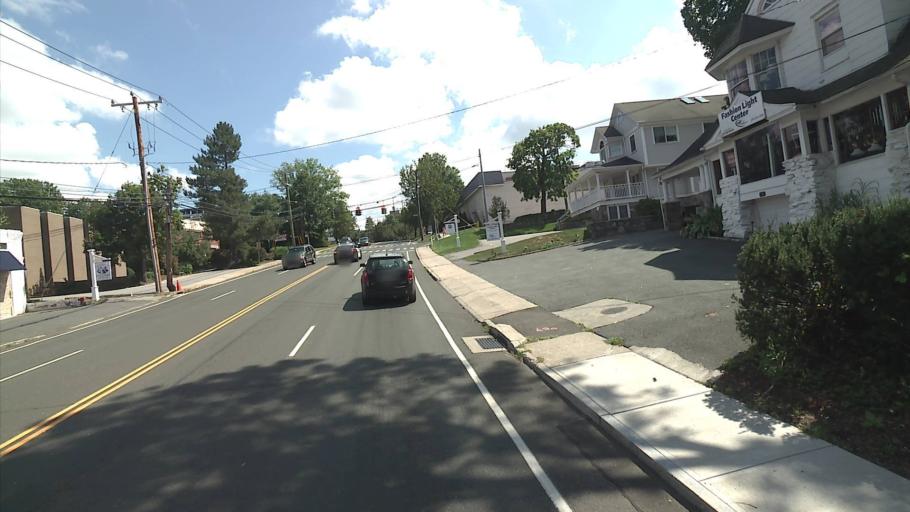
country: US
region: Connecticut
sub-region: Fairfield County
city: Greenwich
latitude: 41.0264
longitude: -73.6323
